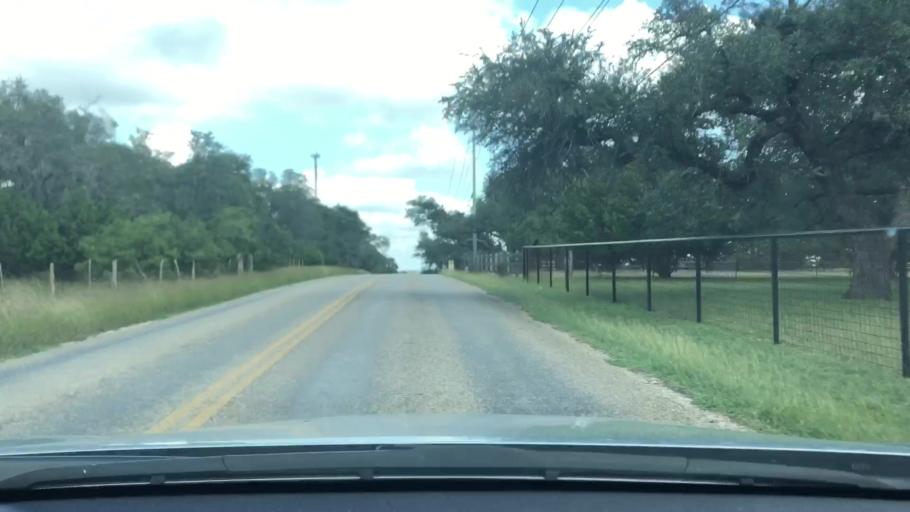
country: US
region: Texas
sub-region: Bexar County
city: Fair Oaks Ranch
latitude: 29.7854
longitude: -98.6394
